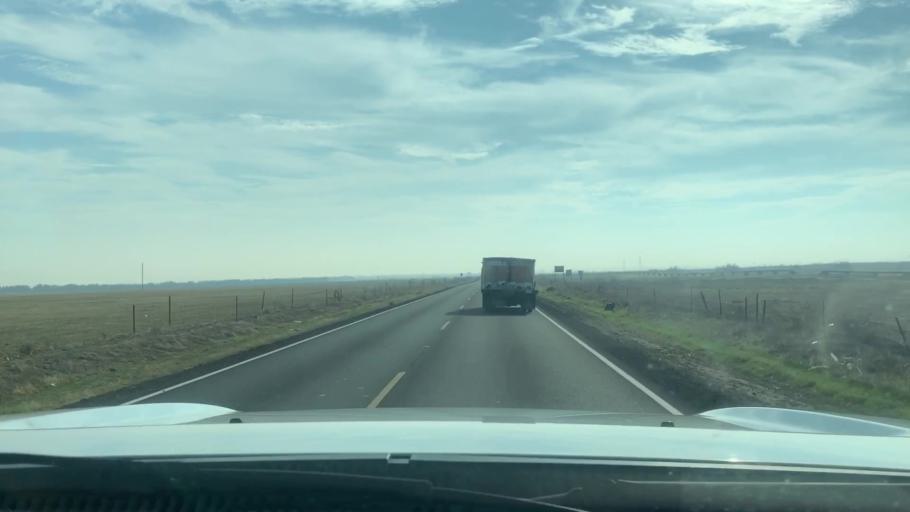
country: US
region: California
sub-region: Kern County
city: Lost Hills
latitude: 35.5546
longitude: -119.7935
